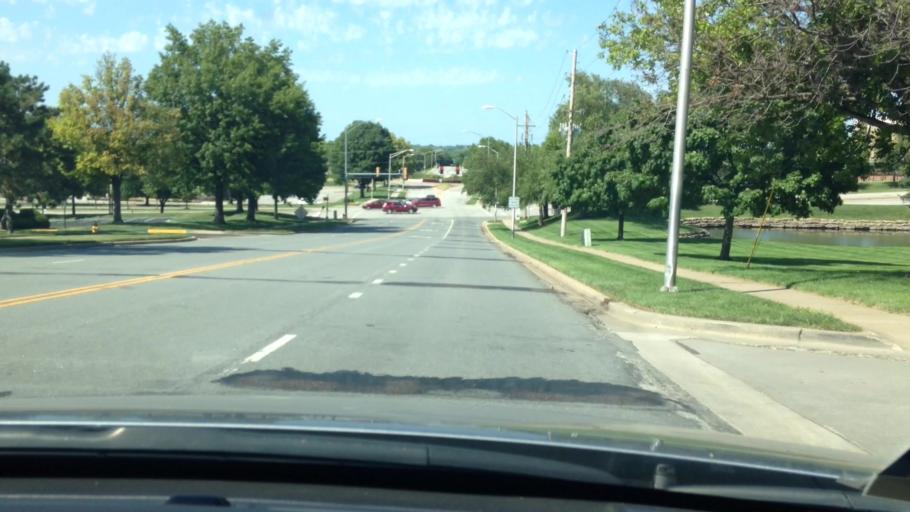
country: US
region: Kansas
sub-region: Johnson County
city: Overland Park
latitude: 38.9262
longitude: -94.6582
